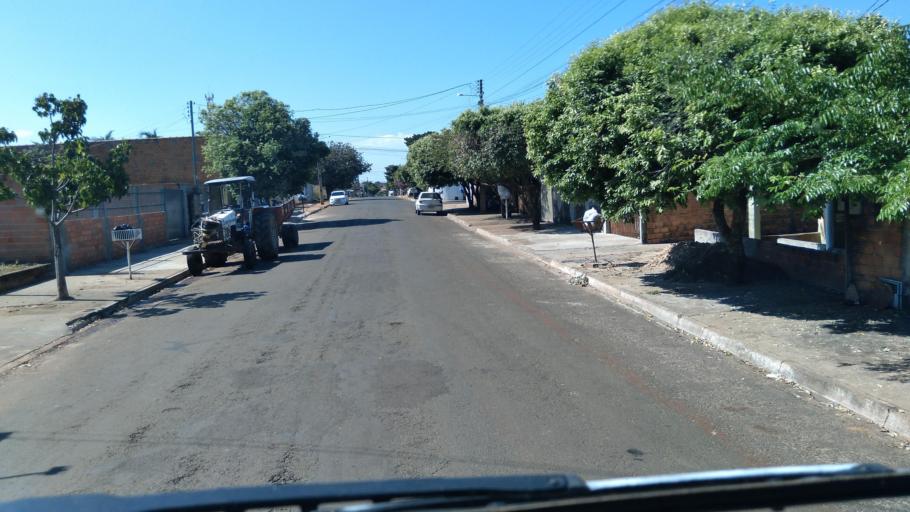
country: BR
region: Goias
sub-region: Mineiros
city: Mineiros
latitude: -17.5706
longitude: -52.5678
